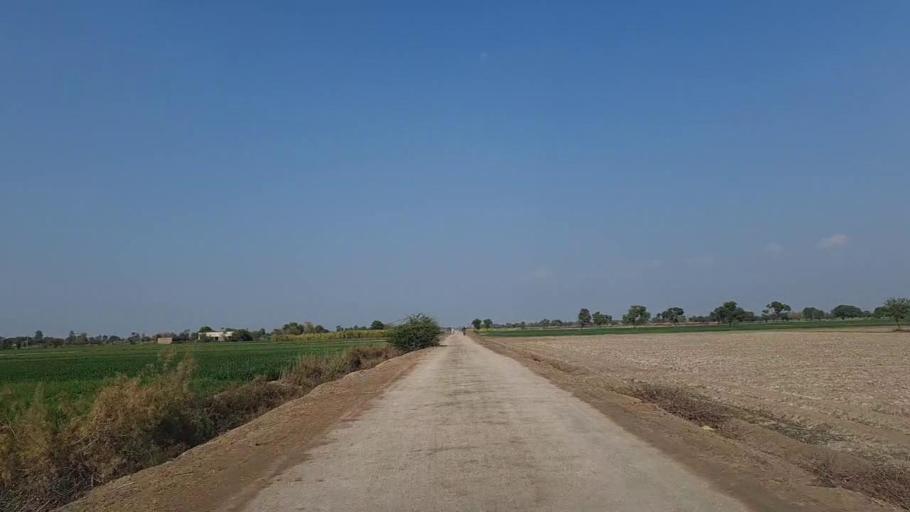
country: PK
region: Sindh
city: Jam Sahib
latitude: 26.2847
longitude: 68.5830
